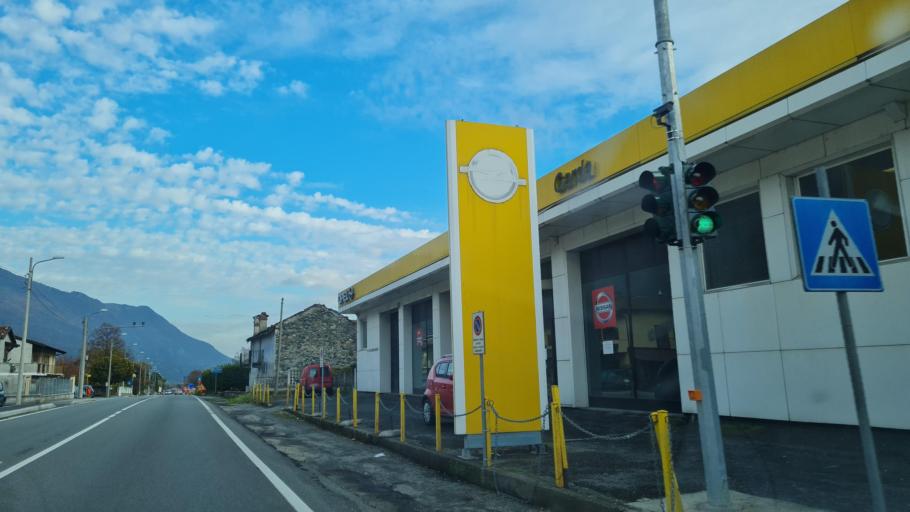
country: IT
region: Piedmont
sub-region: Provincia di Torino
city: Chianocco
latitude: 45.1366
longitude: 7.1683
